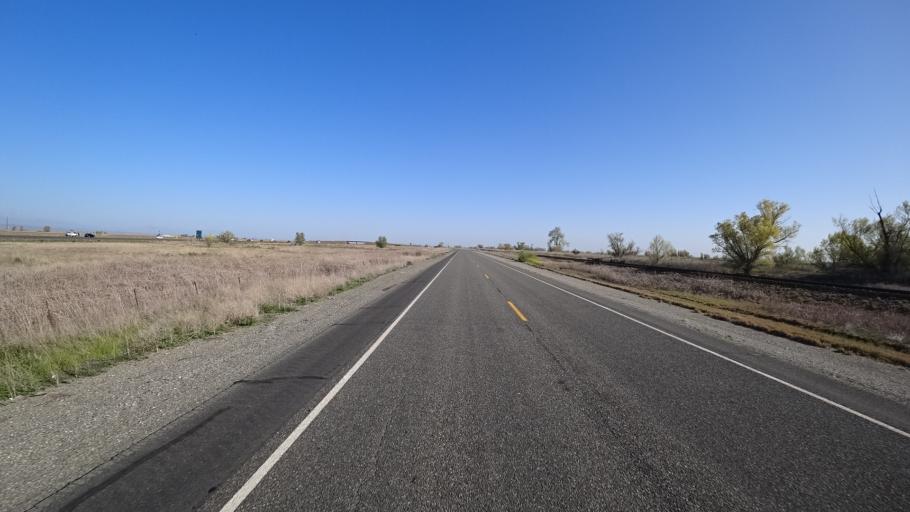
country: US
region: California
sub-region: Colusa County
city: Maxwell
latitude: 39.3986
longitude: -122.1925
